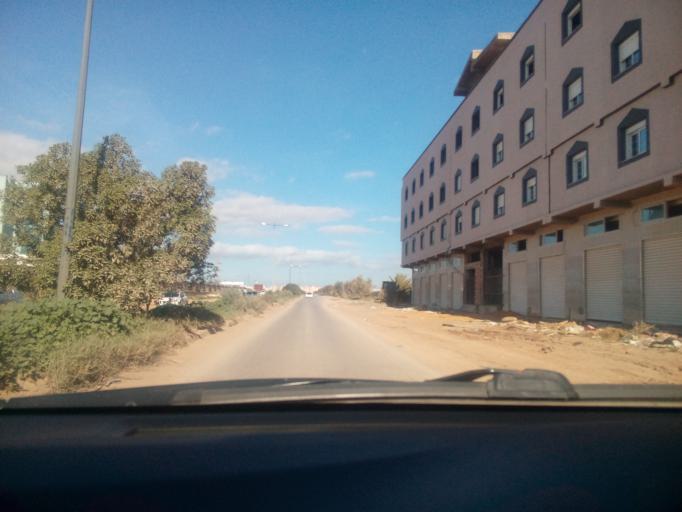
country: DZ
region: Oran
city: Sidi ech Chahmi
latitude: 35.6559
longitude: -0.5678
